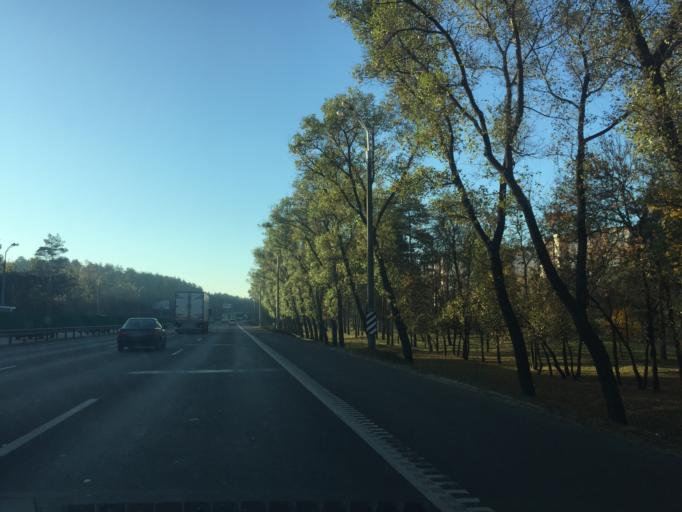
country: BY
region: Minsk
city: Vyaliki Trastsyanets
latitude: 53.8871
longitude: 27.6950
